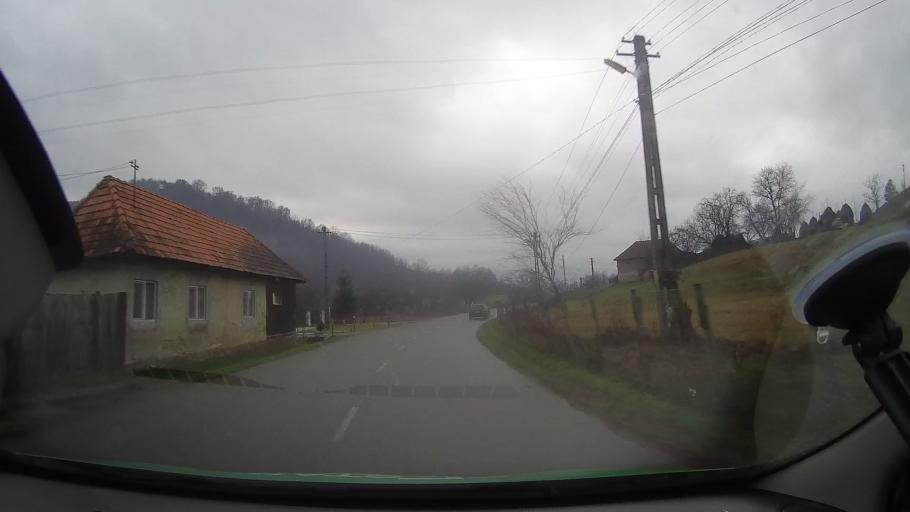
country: RO
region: Hunedoara
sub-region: Comuna Tomesti
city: Tomesti
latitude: 46.1986
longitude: 22.6478
